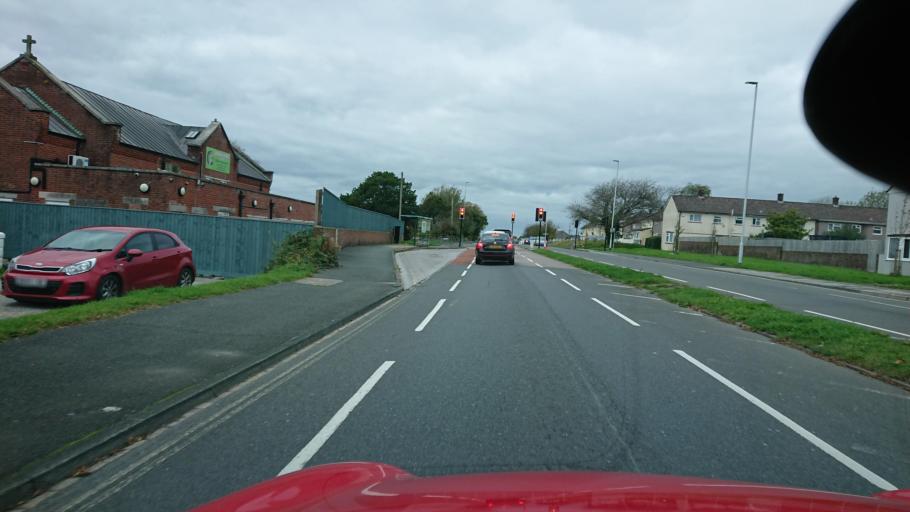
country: GB
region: England
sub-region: Plymouth
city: Plymouth
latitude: 50.4113
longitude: -4.1403
